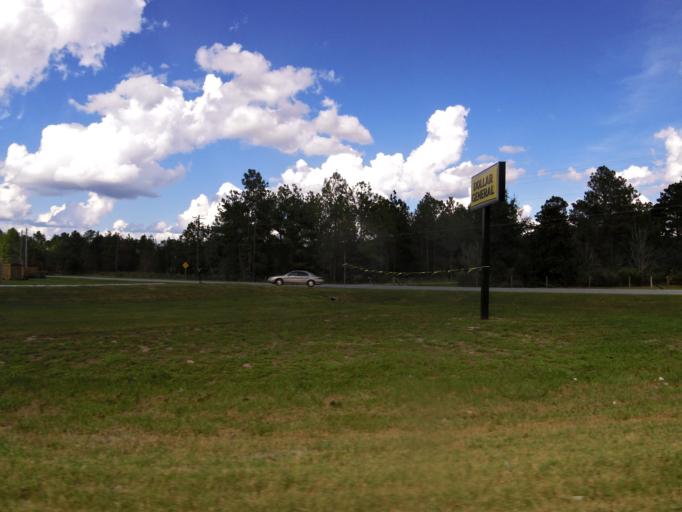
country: US
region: Georgia
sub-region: Echols County
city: Statenville
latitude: 30.7725
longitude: -83.1429
